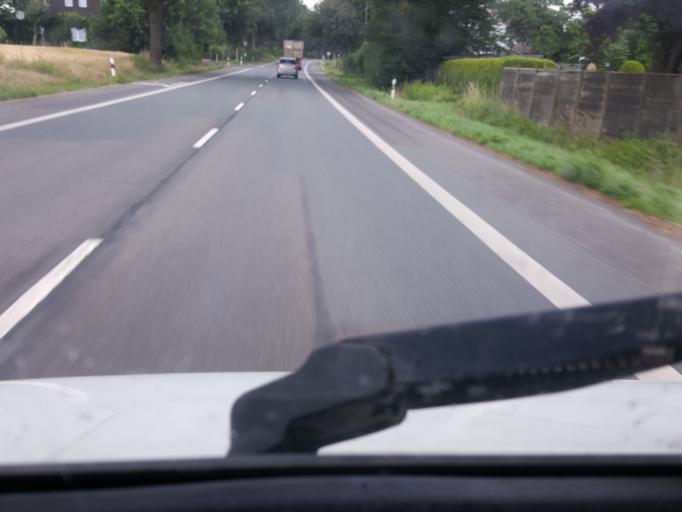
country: DE
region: North Rhine-Westphalia
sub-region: Regierungsbezirk Detmold
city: Minden
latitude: 52.3246
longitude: 8.9217
